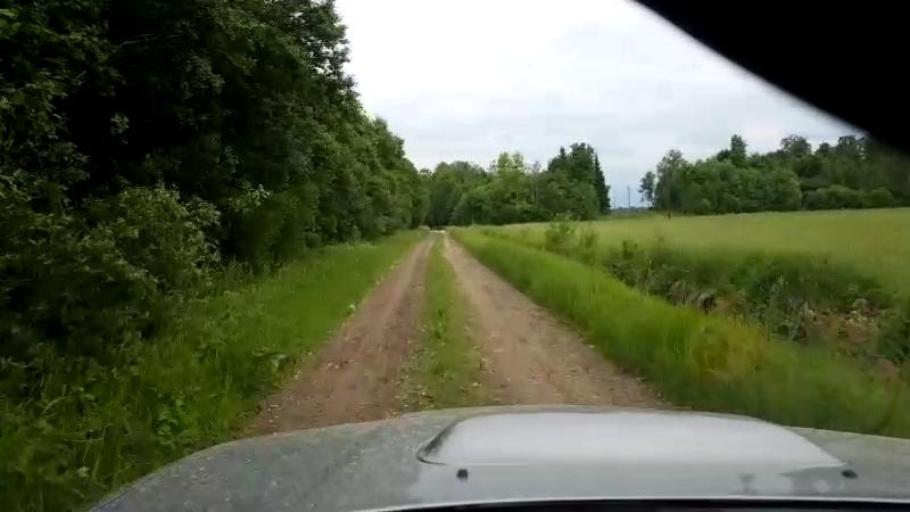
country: EE
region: Paernumaa
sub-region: Tootsi vald
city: Tootsi
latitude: 58.5958
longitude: 24.6628
